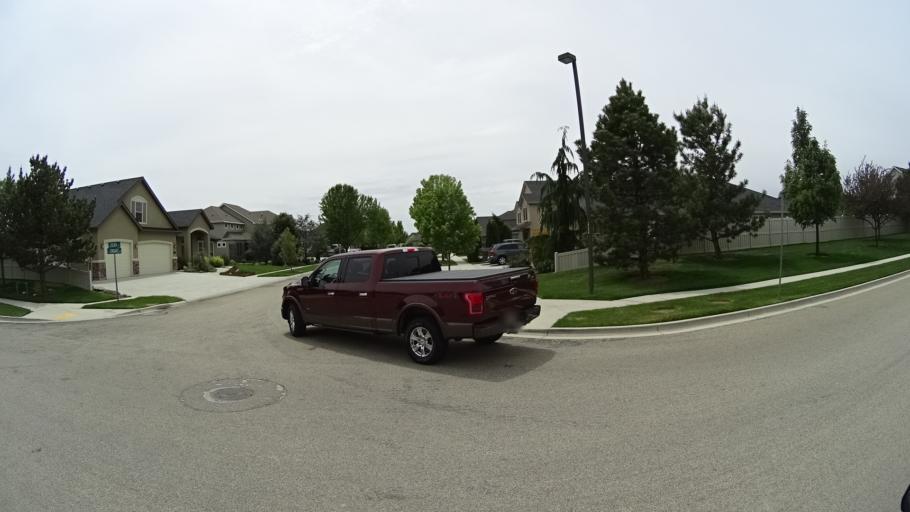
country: US
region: Idaho
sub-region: Ada County
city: Meridian
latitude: 43.5666
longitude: -116.3525
